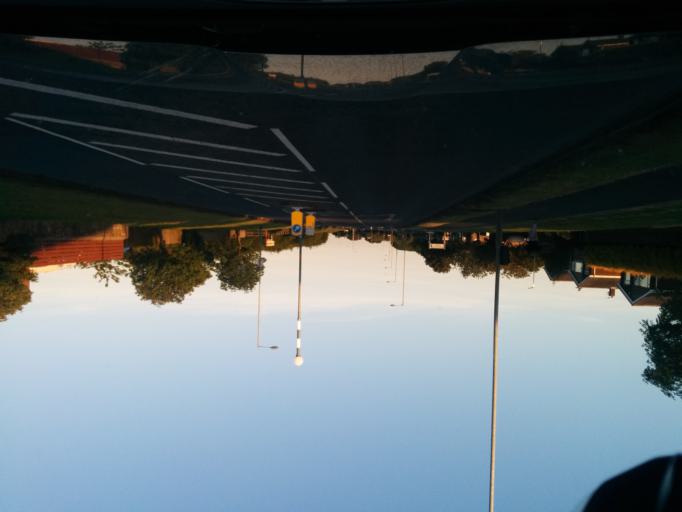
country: GB
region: England
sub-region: Northumberland
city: Newbiggin-by-the-Sea
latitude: 55.1712
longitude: -1.5454
